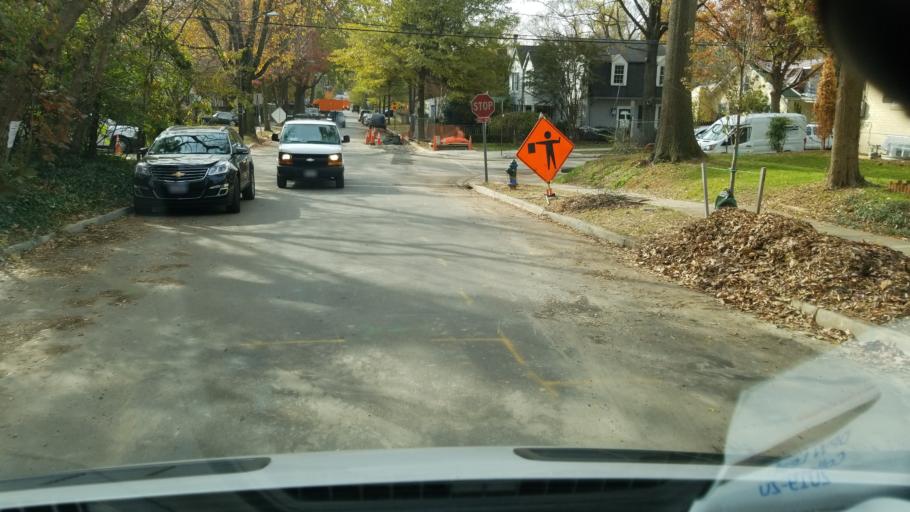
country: US
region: Maryland
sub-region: Montgomery County
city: Friendship Village
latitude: 38.9501
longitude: -77.0943
